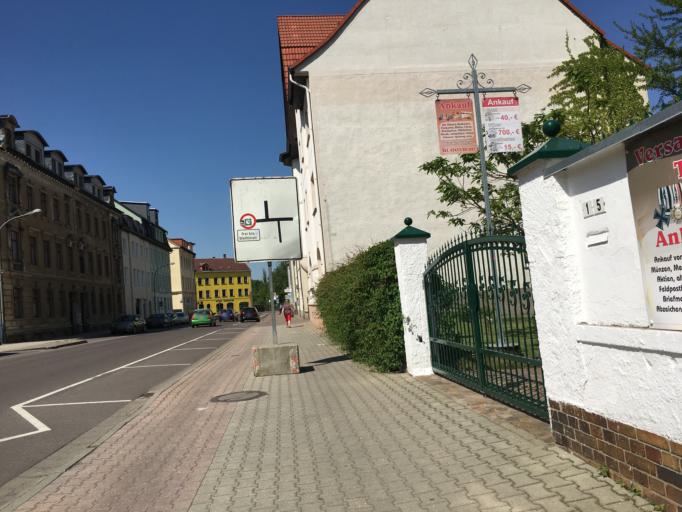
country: DE
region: Saxony
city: Borna
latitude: 51.1205
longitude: 12.4940
